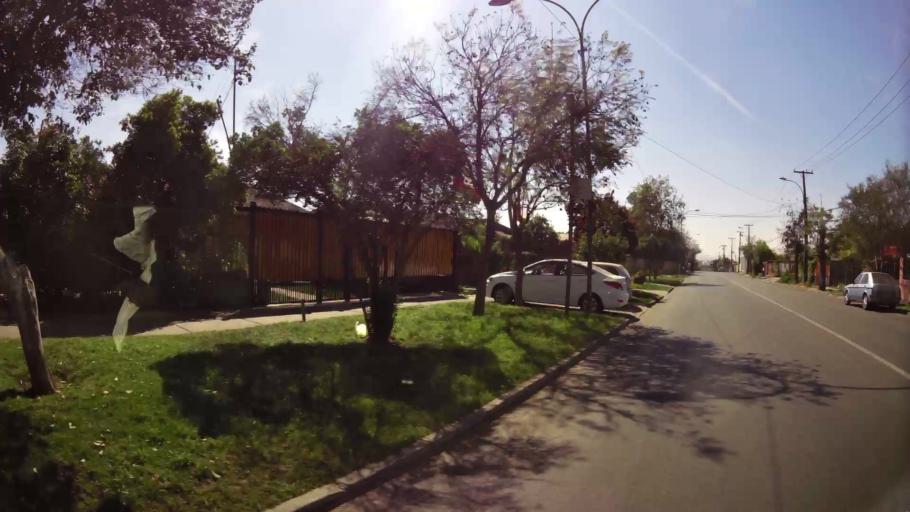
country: CL
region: Santiago Metropolitan
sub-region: Provincia de Santiago
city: Lo Prado
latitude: -33.4996
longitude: -70.7286
